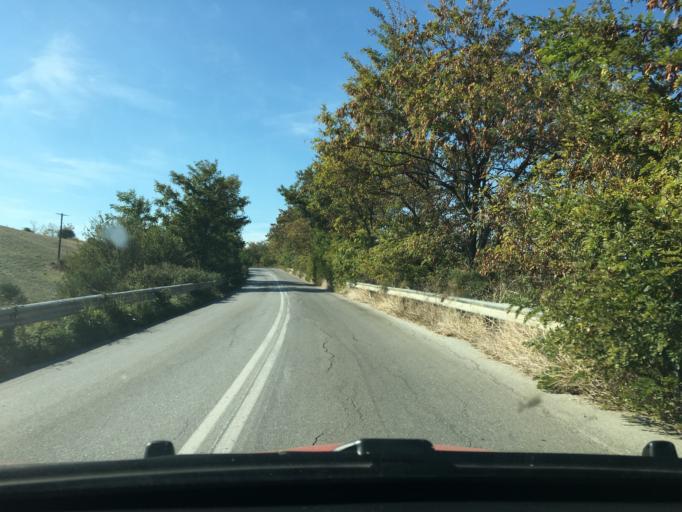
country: GR
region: Central Macedonia
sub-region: Nomos Chalkidikis
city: Nea Roda
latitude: 40.3845
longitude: 23.9036
